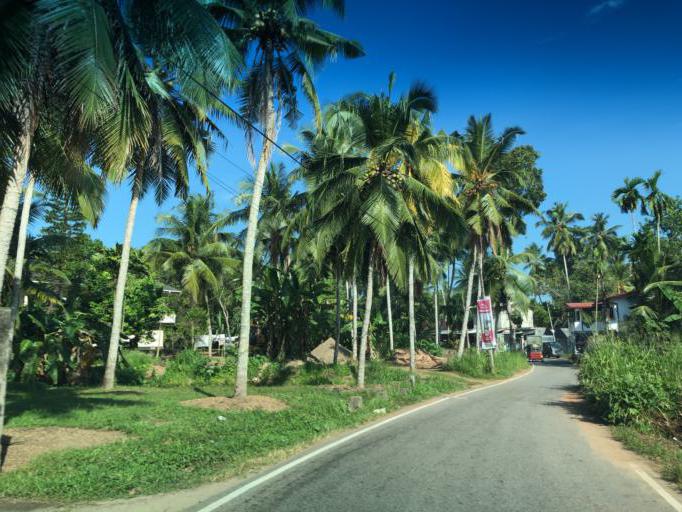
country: LK
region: Western
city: Homagama
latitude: 6.8005
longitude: 79.9809
